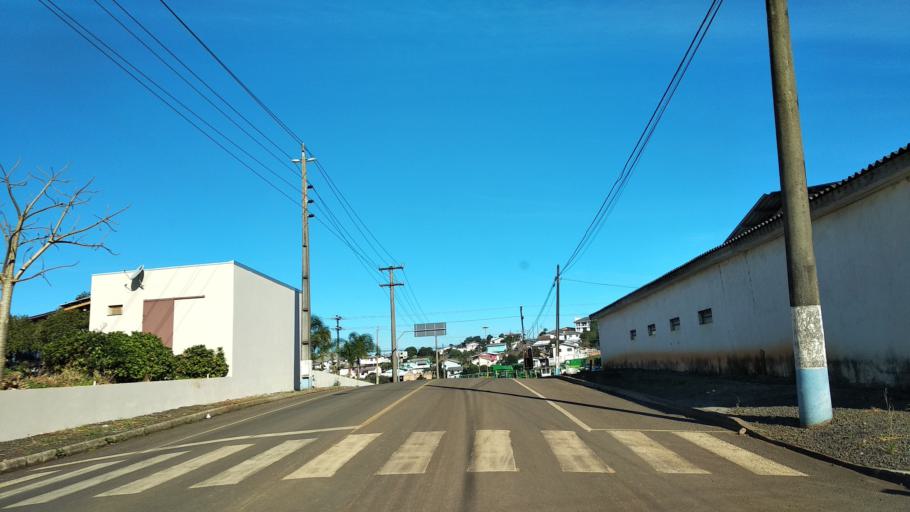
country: BR
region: Santa Catarina
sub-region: Campos Novos
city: Campos Novos
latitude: -27.3868
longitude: -51.2085
